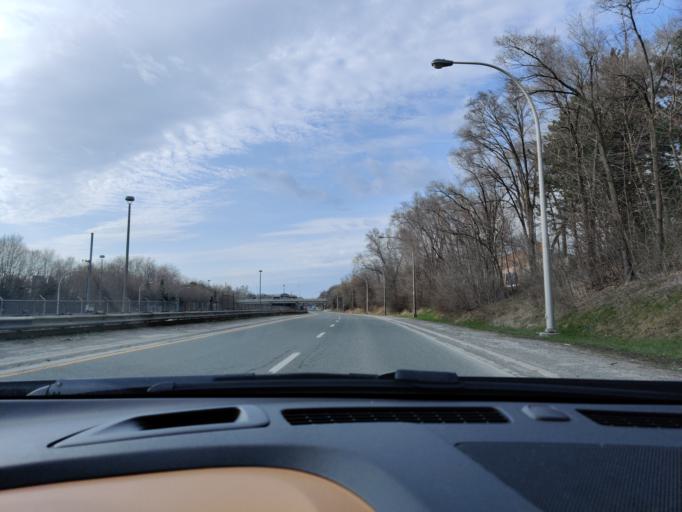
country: CA
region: Ontario
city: Toronto
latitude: 43.7050
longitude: -79.4381
